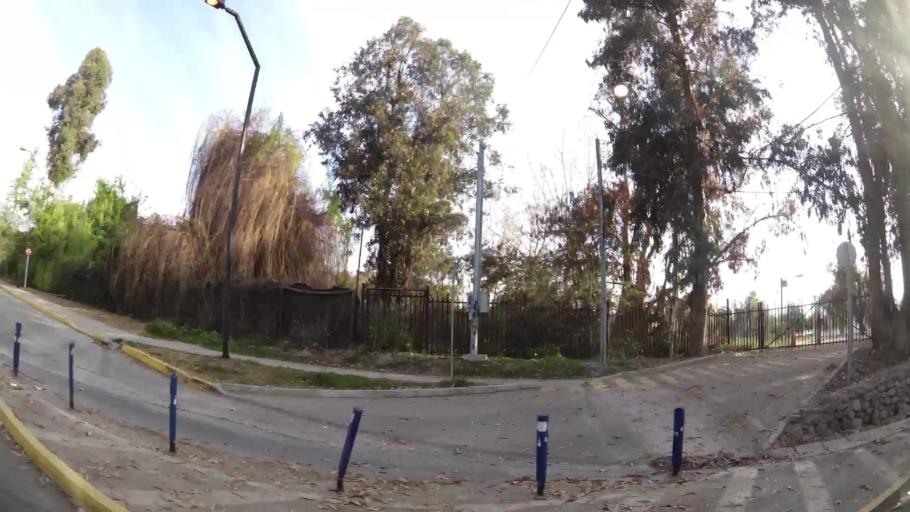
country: CL
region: Santiago Metropolitan
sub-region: Provincia de Santiago
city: Villa Presidente Frei, Nunoa, Santiago, Chile
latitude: -33.5007
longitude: -70.5485
